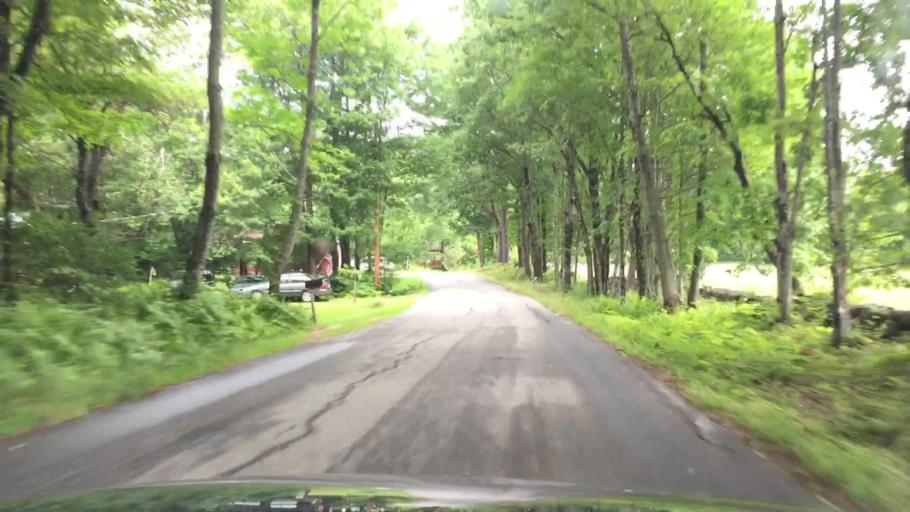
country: US
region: New Hampshire
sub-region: Carroll County
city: Sandwich
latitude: 43.8015
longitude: -71.4725
